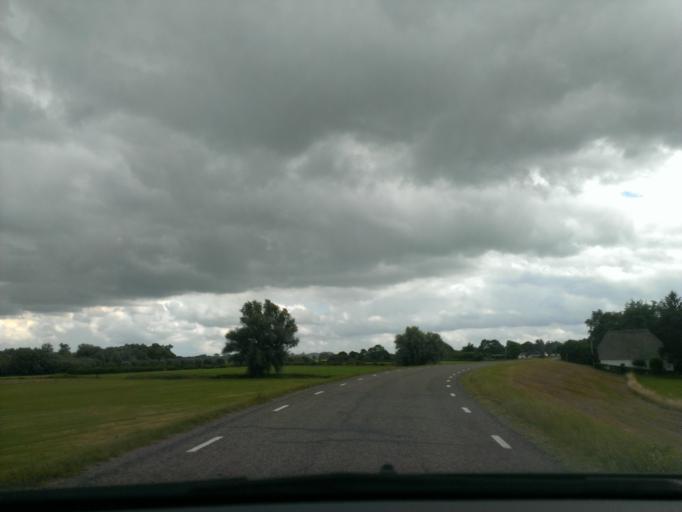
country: NL
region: Overijssel
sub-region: Gemeente Olst-Wijhe
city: Olst
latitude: 52.2916
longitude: 6.1004
